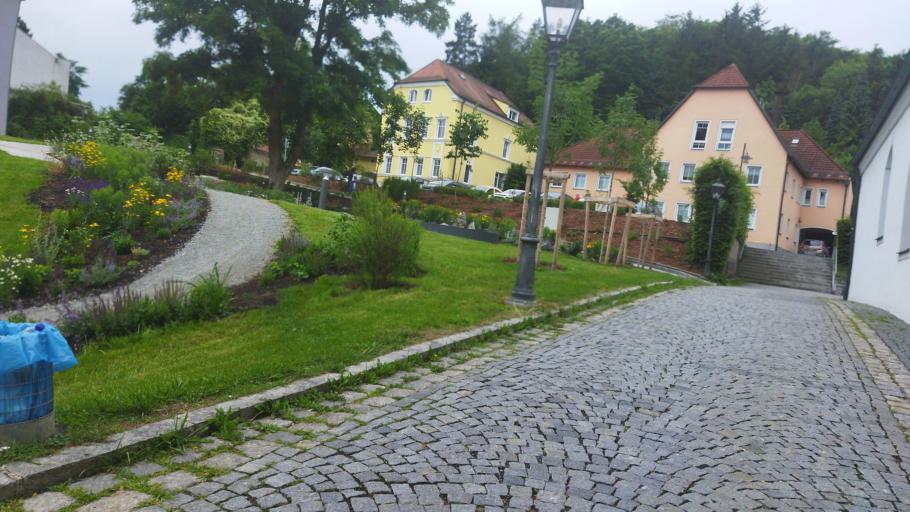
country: DE
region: Bavaria
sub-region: Upper Palatinate
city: Worth an der Donau
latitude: 49.0002
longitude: 12.3998
